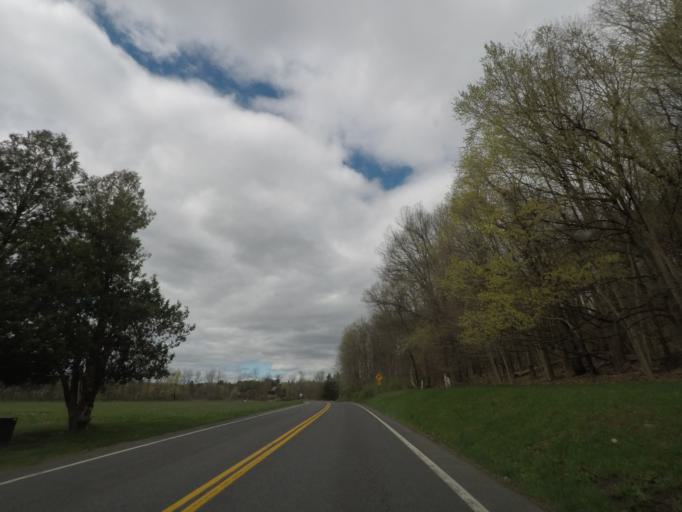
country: US
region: New York
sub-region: Columbia County
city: Chatham
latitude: 42.3139
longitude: -73.6267
